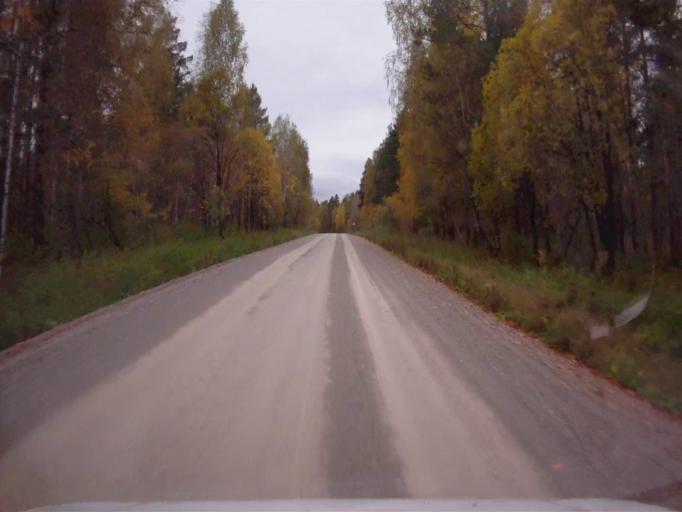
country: RU
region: Chelyabinsk
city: Nyazepetrovsk
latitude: 56.0643
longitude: 59.4419
